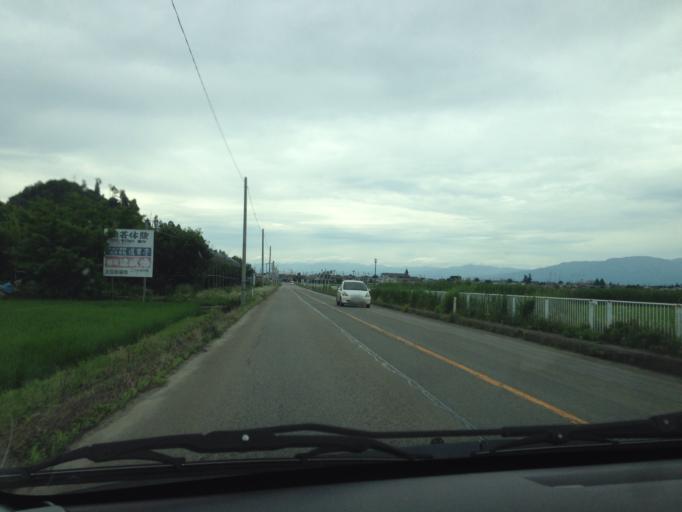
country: JP
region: Fukushima
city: Kitakata
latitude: 37.4418
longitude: 139.8813
